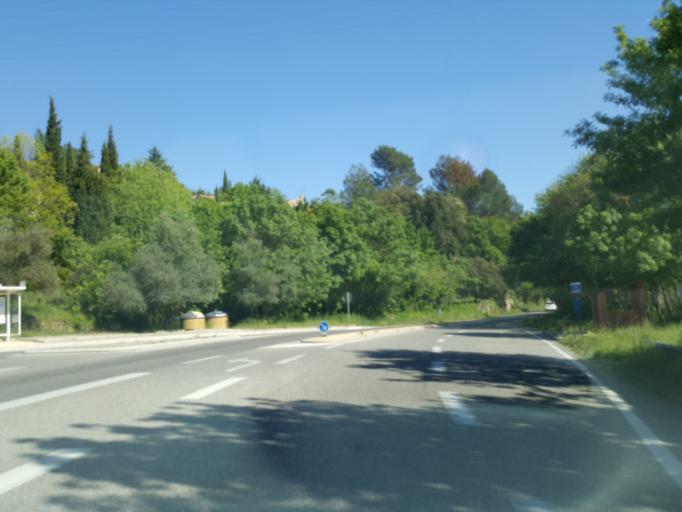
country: FR
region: Provence-Alpes-Cote d'Azur
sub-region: Departement du Var
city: Belgentier
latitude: 43.2541
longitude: 5.9911
